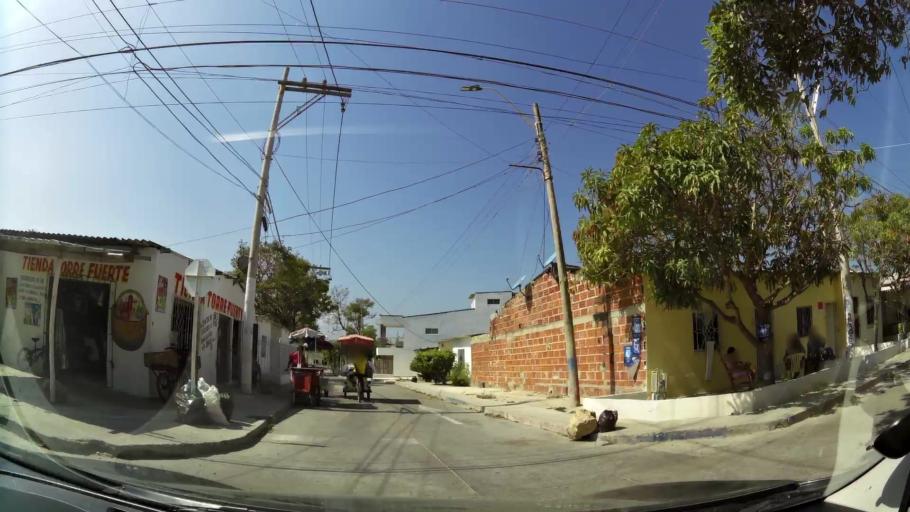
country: CO
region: Atlantico
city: Barranquilla
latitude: 10.9718
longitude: -74.8361
